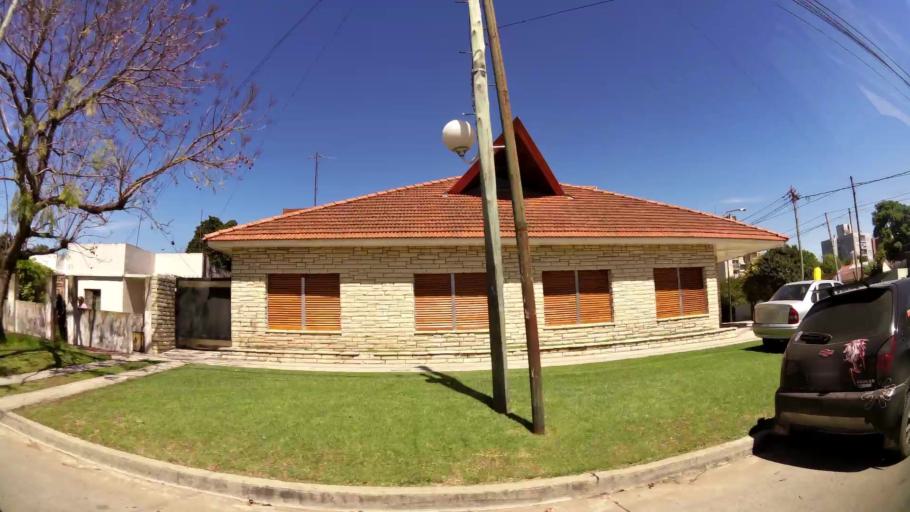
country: AR
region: Buenos Aires
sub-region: Partido de Quilmes
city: Quilmes
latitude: -34.7275
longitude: -58.2870
